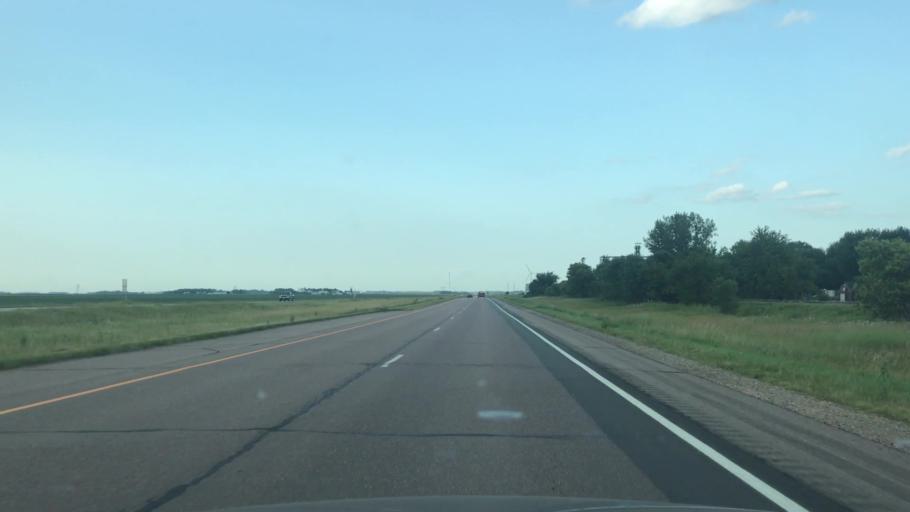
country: US
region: Minnesota
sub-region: Nobles County
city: Worthington
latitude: 43.7000
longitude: -95.4693
